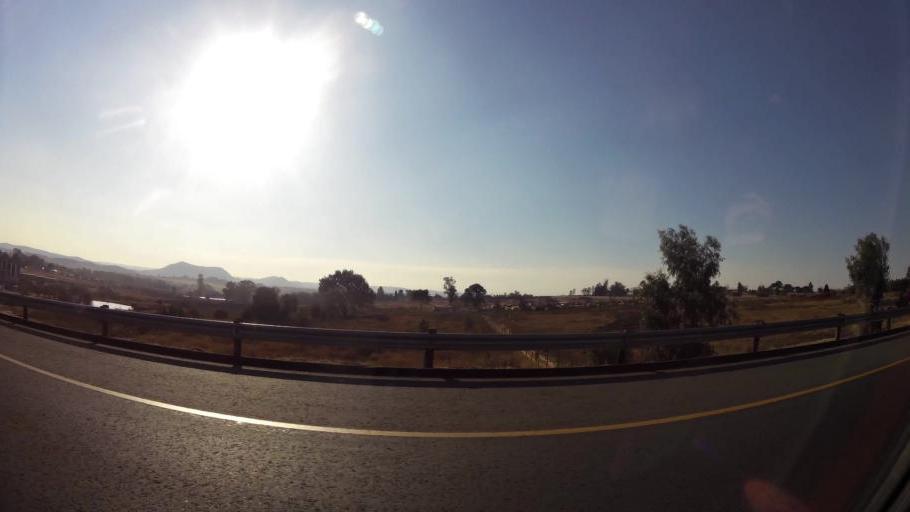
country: ZA
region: Gauteng
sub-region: West Rand District Municipality
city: Muldersdriseloop
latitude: -26.0136
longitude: 27.8767
